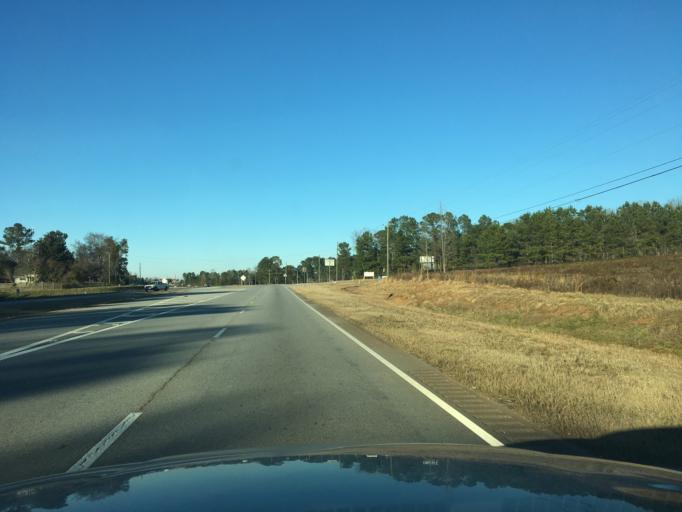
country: US
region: Georgia
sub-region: Carroll County
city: Carrollton
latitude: 33.5034
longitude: -85.0803
